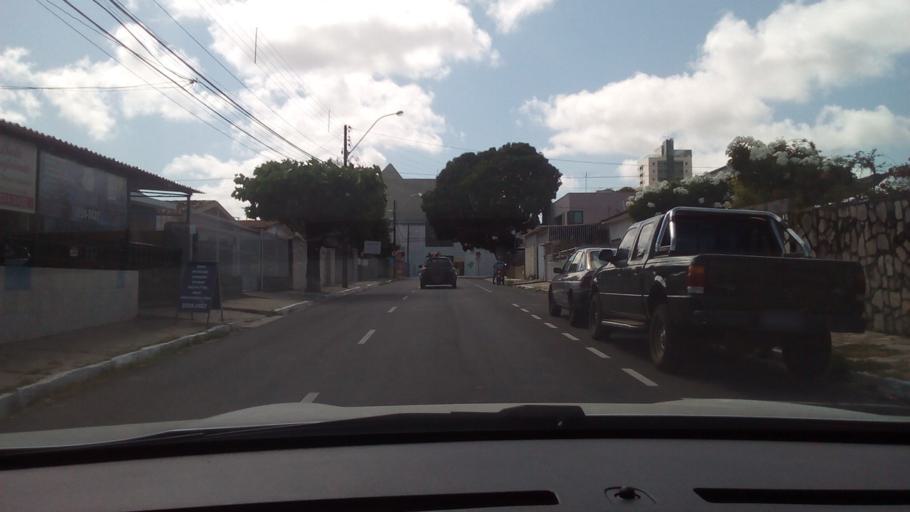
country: BR
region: Paraiba
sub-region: Joao Pessoa
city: Joao Pessoa
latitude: -7.1222
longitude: -34.8401
